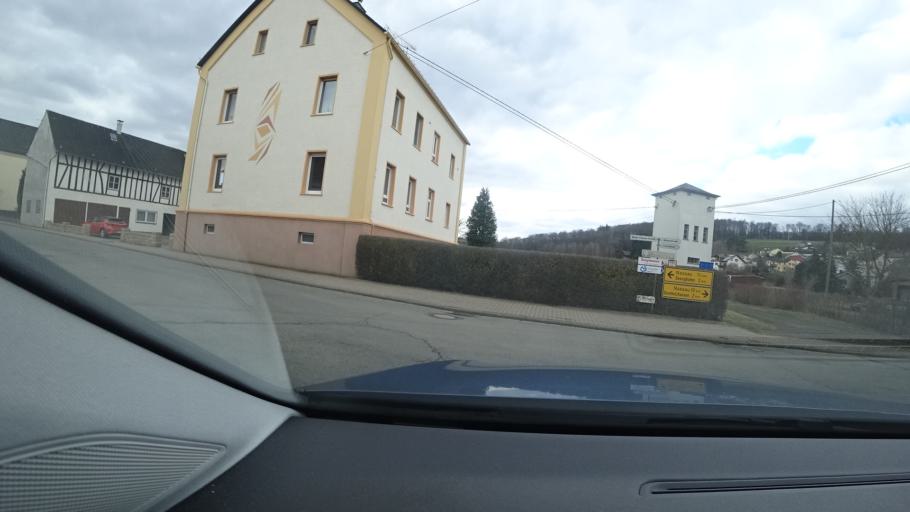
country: DE
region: Rheinland-Pfalz
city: Geisig
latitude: 50.2541
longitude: 7.7911
